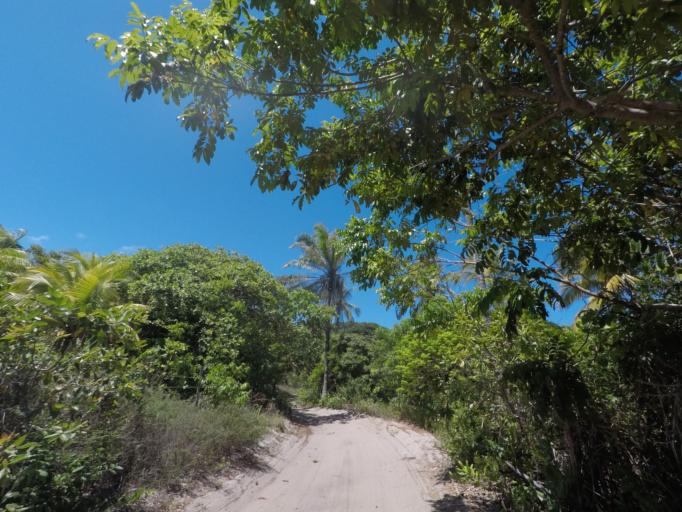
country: BR
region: Bahia
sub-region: Marau
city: Marau
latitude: -14.0077
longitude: -38.9450
